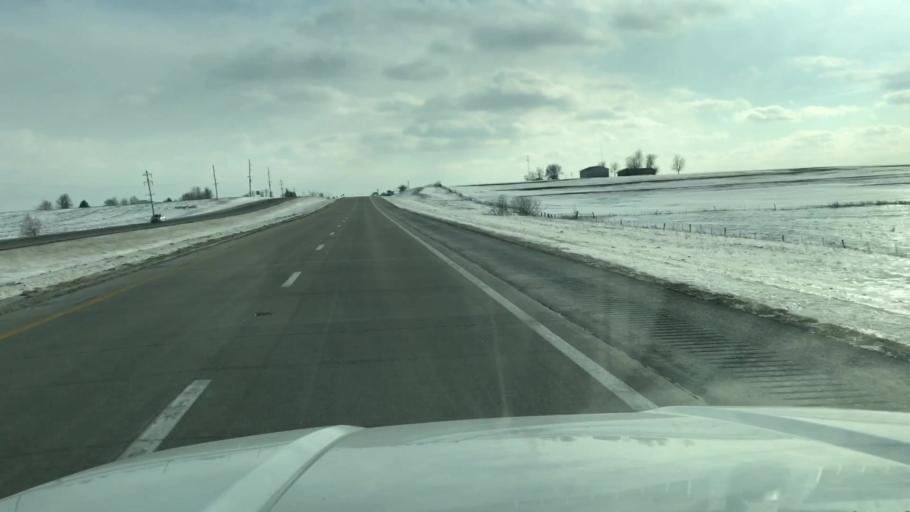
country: US
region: Missouri
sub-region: Nodaway County
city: Maryville
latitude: 40.2641
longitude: -94.8670
